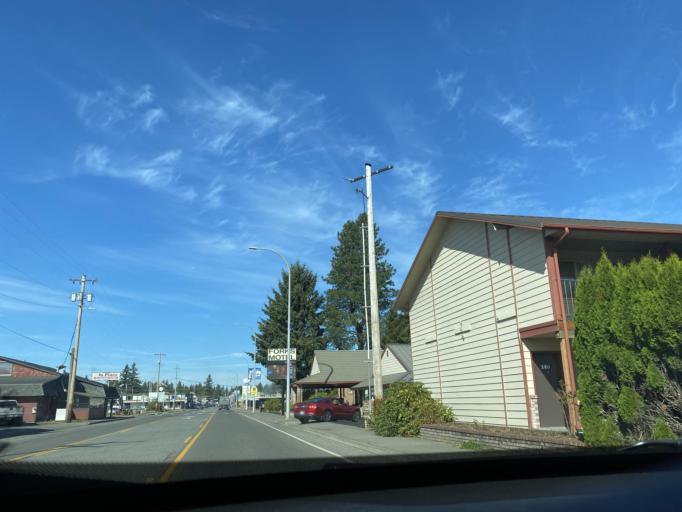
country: US
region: Washington
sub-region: Clallam County
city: Forks
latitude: 47.9471
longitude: -124.3854
